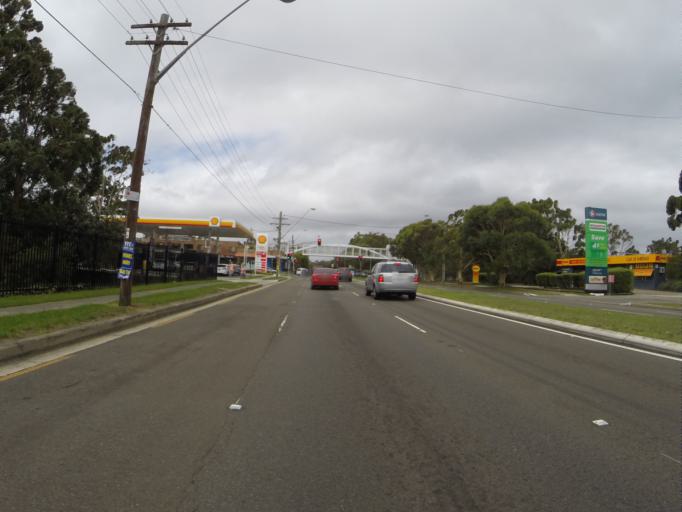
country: AU
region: New South Wales
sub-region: Sutherland Shire
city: Heathcote
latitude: -34.0883
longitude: 151.0068
